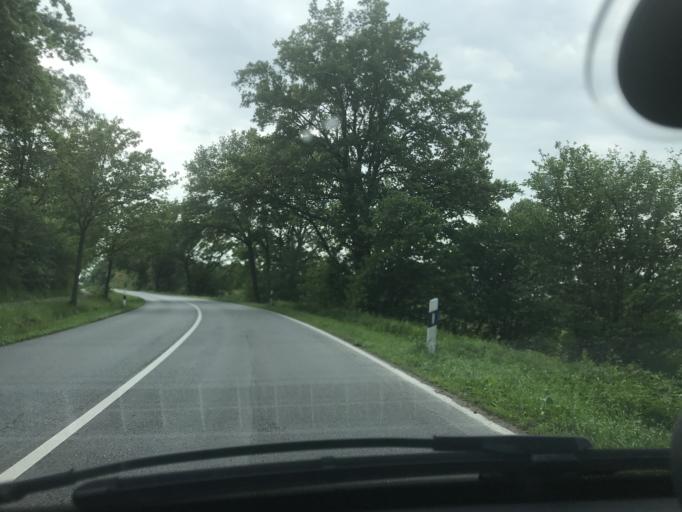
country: DE
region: Schleswig-Holstein
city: Trittau
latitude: 53.6157
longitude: 10.3864
